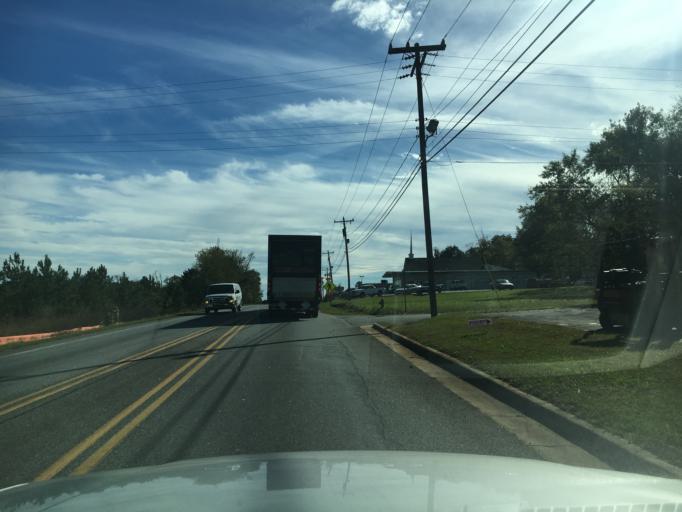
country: US
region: North Carolina
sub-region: Rutherford County
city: Rutherfordton
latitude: 35.3682
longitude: -81.9420
